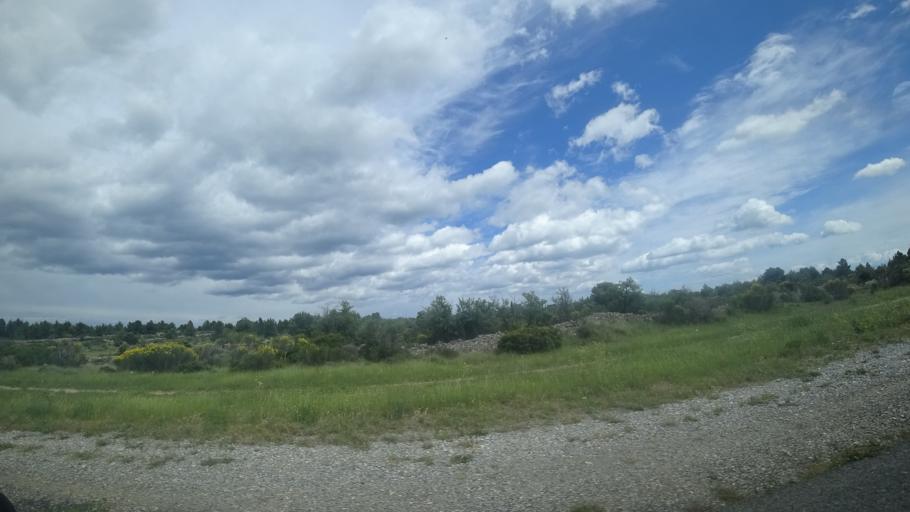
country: FR
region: Languedoc-Roussillon
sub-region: Departement de l'Aude
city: Leucate
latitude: 42.9230
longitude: 3.0178
